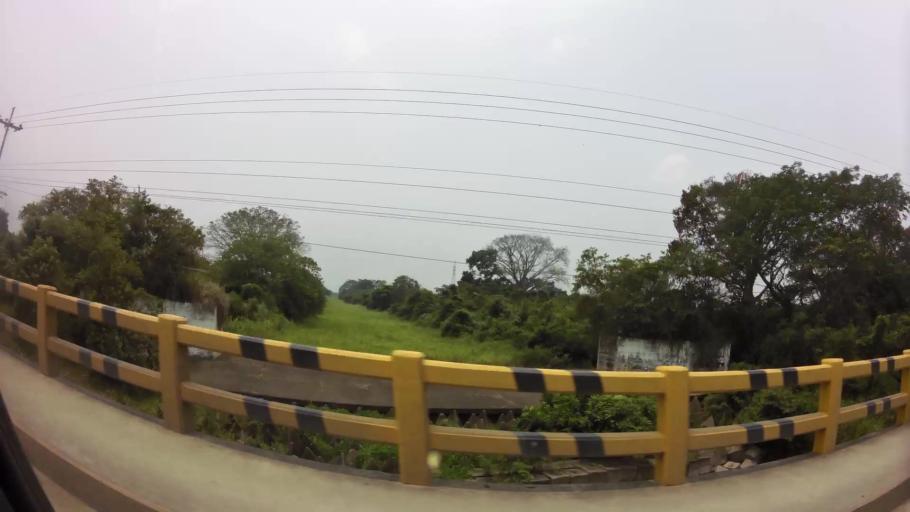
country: HN
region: Yoro
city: El Progreso
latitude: 15.4118
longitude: -87.8475
